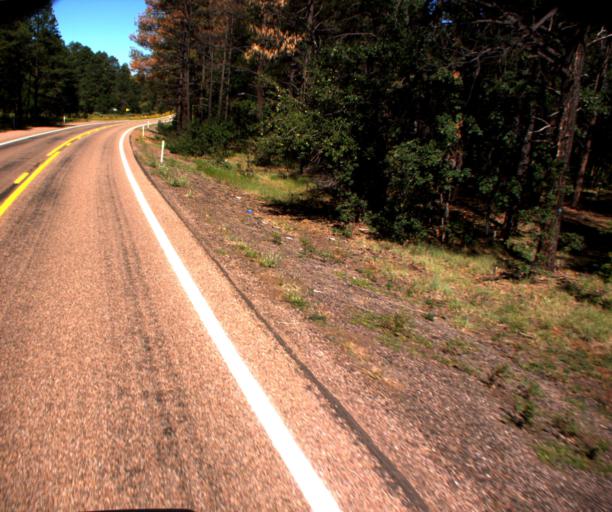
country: US
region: Arizona
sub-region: Navajo County
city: Pinetop-Lakeside
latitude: 34.0723
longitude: -109.8439
